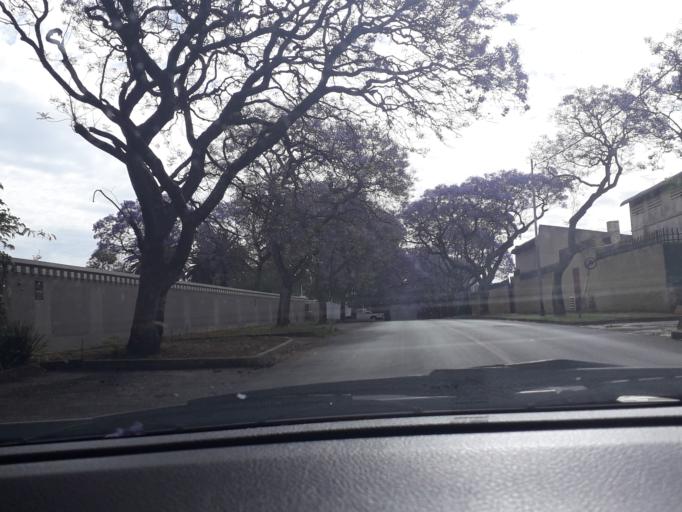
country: ZA
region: Gauteng
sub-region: City of Johannesburg Metropolitan Municipality
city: Johannesburg
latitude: -26.1584
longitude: 28.0641
